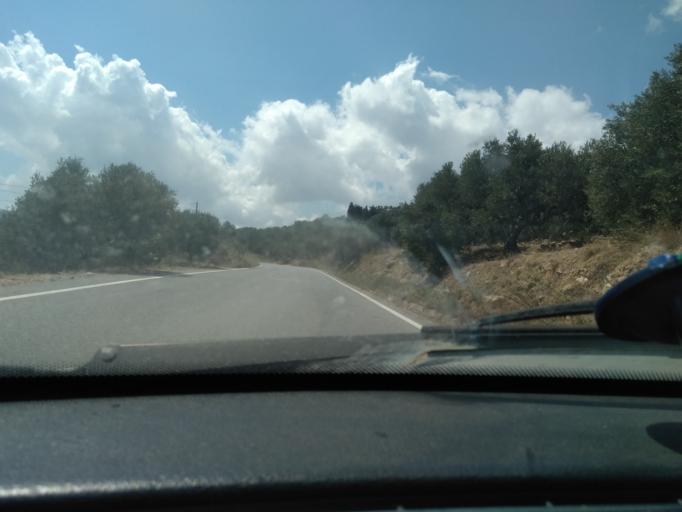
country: GR
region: Crete
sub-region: Nomos Lasithiou
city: Siteia
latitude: 35.1380
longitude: 26.0756
